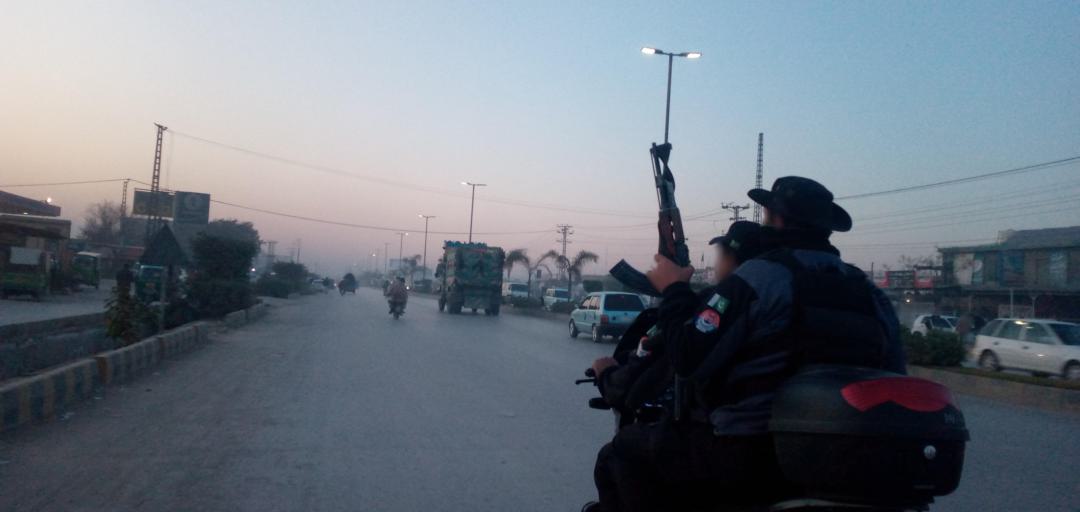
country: PK
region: Khyber Pakhtunkhwa
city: Peshawar
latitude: 34.0298
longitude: 71.6119
